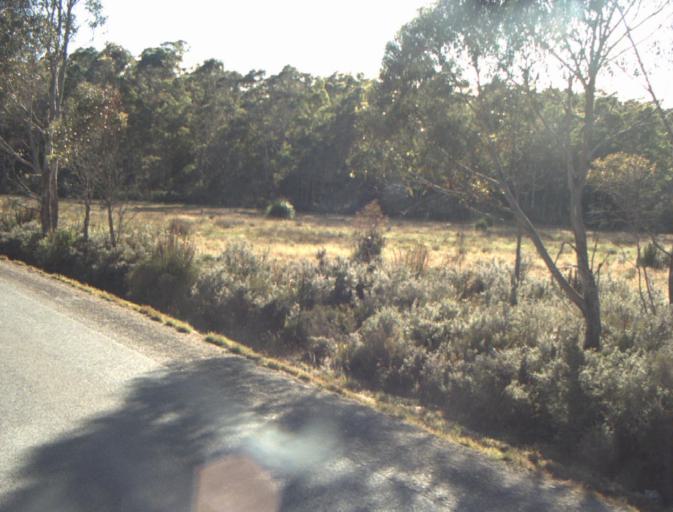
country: AU
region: Tasmania
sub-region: Launceston
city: Mayfield
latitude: -41.3157
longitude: 147.1943
